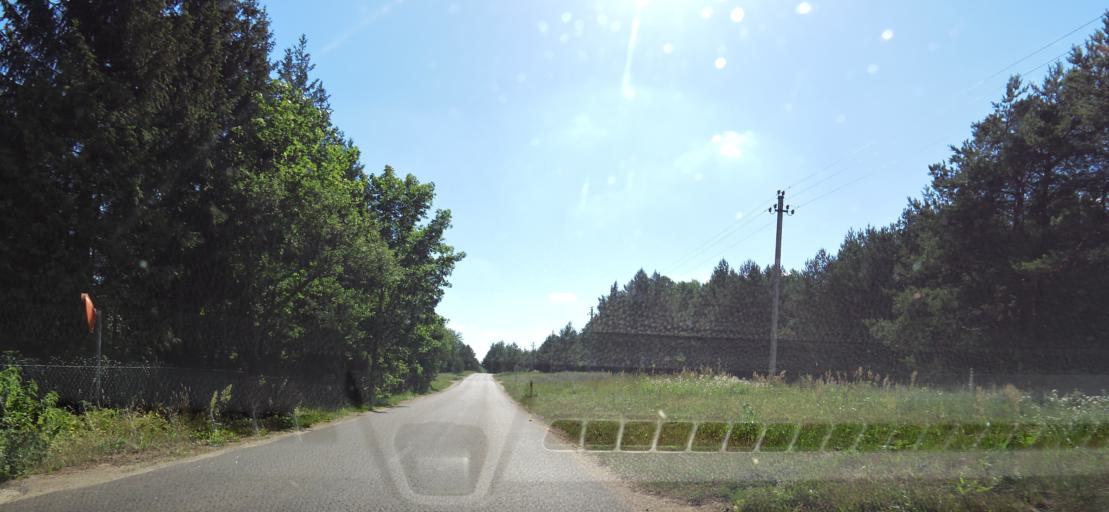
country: LT
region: Vilnius County
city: Rasos
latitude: 54.7590
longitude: 25.3445
